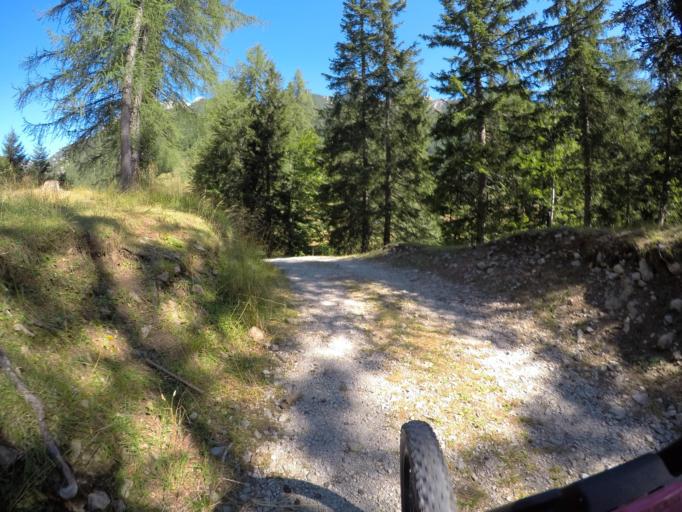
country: IT
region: Friuli Venezia Giulia
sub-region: Provincia di Udine
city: Malborghetto
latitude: 46.4613
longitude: 13.4501
